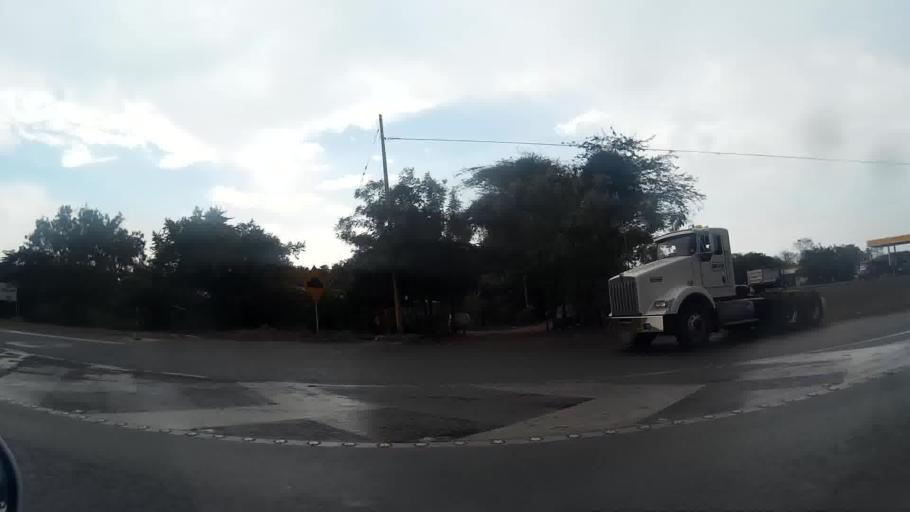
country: CO
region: Magdalena
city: Cienaga
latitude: 11.0118
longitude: -74.2157
